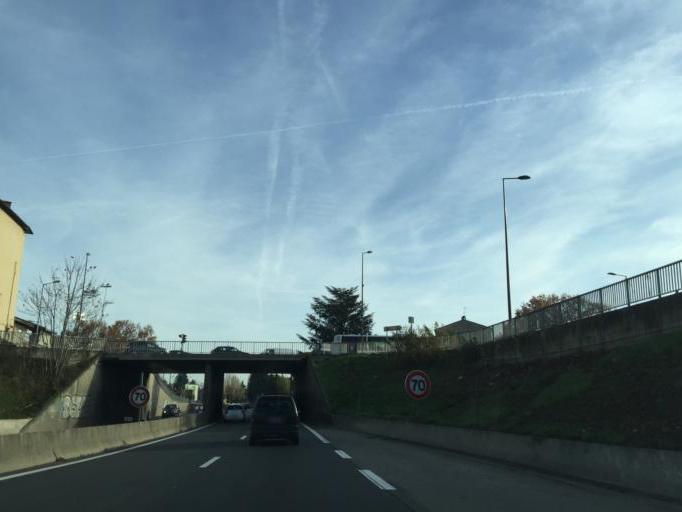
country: FR
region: Rhone-Alpes
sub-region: Departement du Rhone
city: Givors
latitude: 45.5878
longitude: 4.7595
